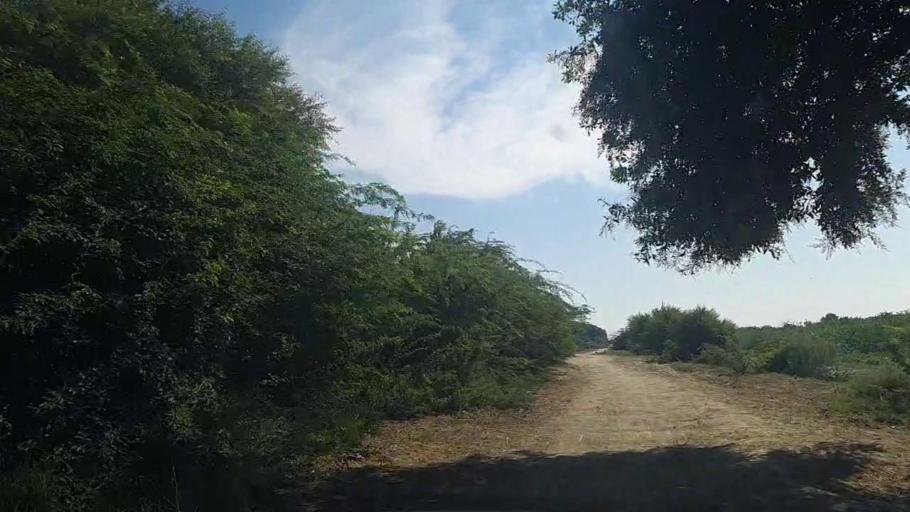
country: PK
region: Sindh
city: Mirpur Batoro
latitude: 24.6611
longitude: 68.1924
